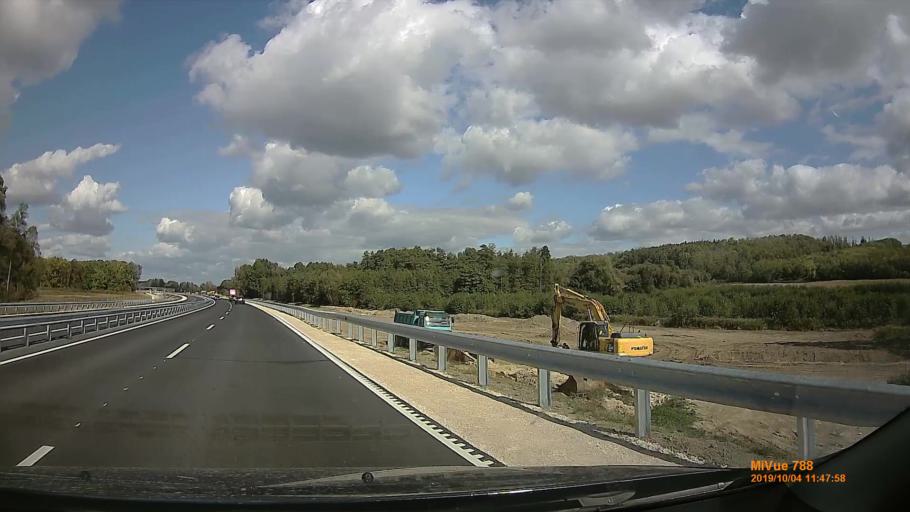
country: HU
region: Somogy
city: Karad
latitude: 46.6563
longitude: 17.7866
